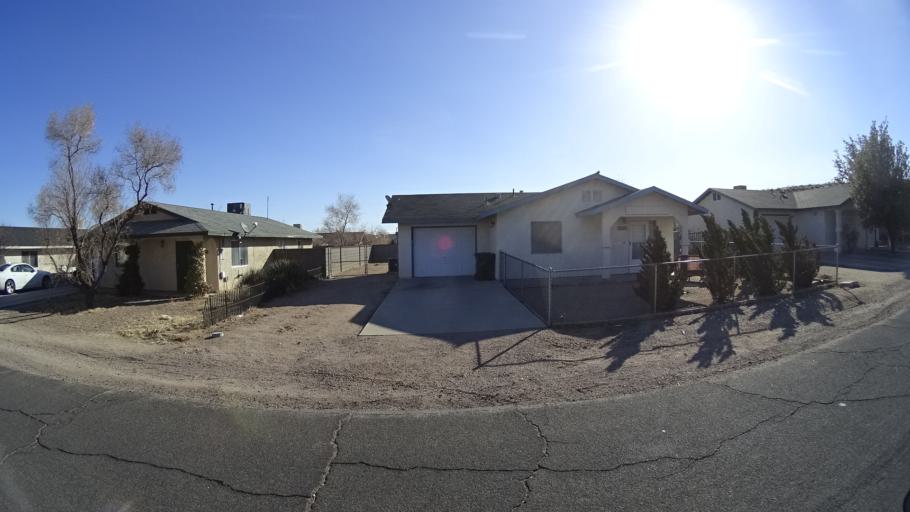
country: US
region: Arizona
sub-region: Mohave County
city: Kingman
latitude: 35.2114
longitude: -114.0102
